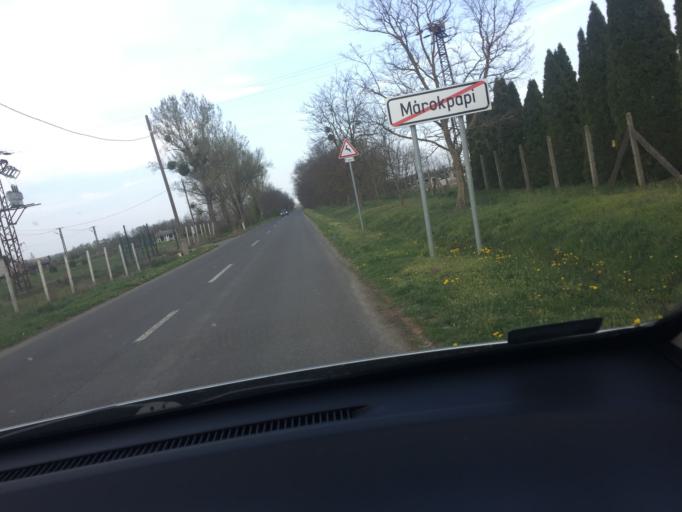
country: HU
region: Szabolcs-Szatmar-Bereg
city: Tarpa
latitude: 48.1533
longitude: 22.5086
